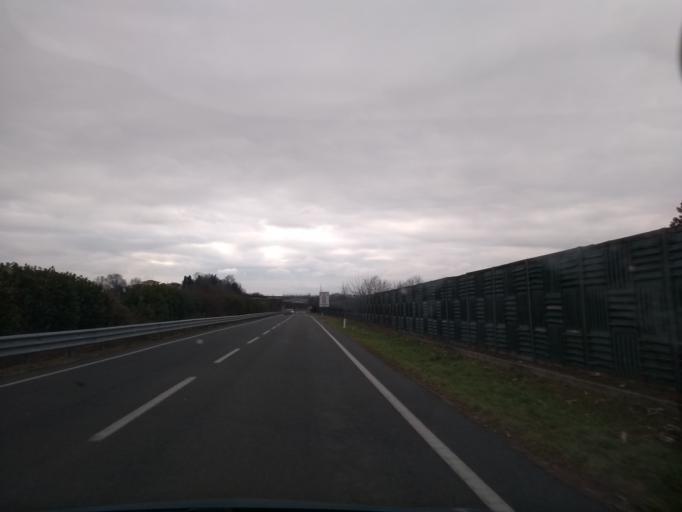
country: IT
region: Piedmont
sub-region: Provincia di Torino
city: Salerano Canavese
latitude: 45.4561
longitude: 7.8529
